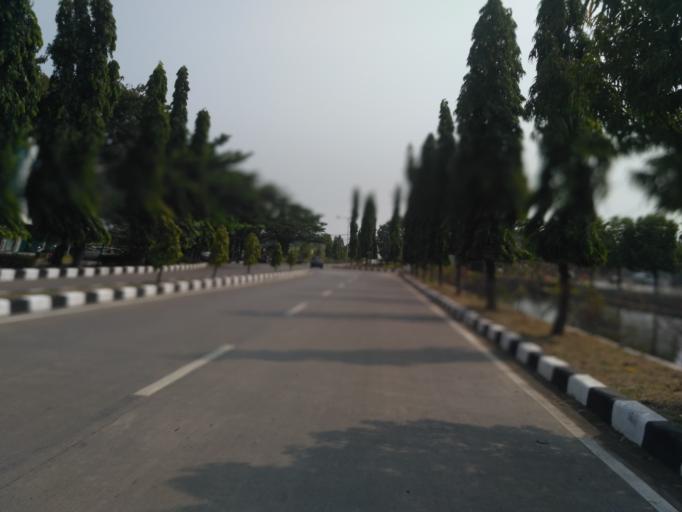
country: ID
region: Central Java
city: Semarang
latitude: -6.9625
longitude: 110.3917
